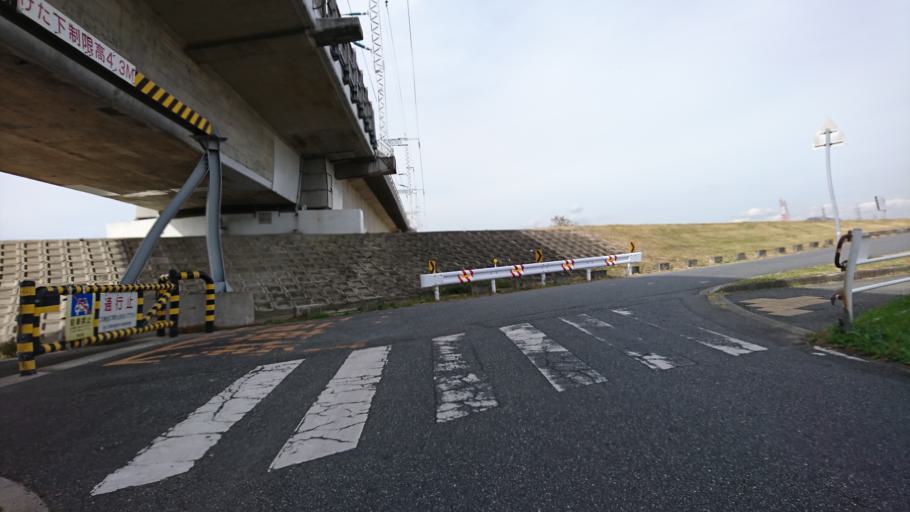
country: JP
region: Hyogo
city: Kakogawacho-honmachi
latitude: 34.7589
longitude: 134.8100
